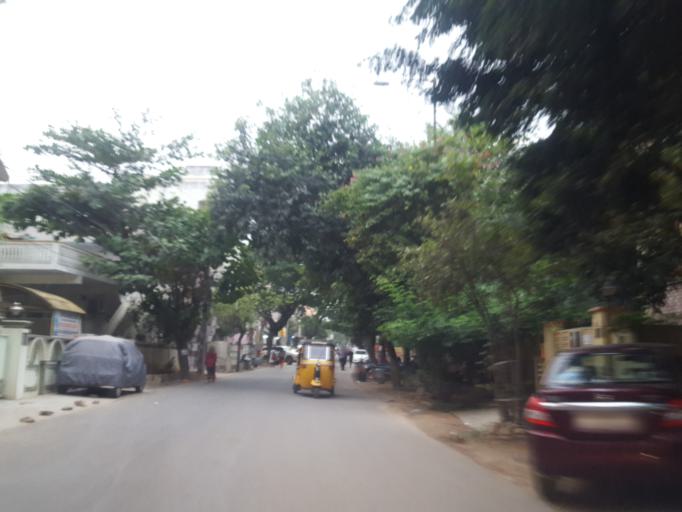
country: IN
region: Telangana
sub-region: Medak
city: Serilingampalle
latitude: 17.4946
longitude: 78.3322
